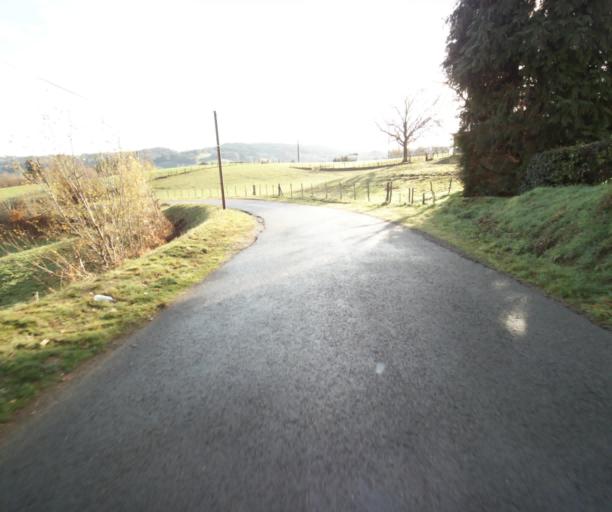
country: FR
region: Limousin
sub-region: Departement de la Correze
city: Saint-Mexant
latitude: 45.2419
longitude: 1.6329
